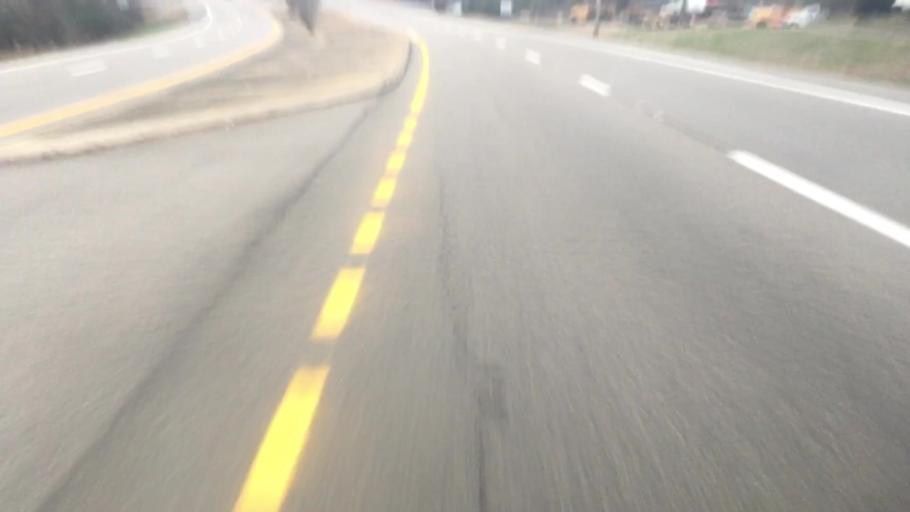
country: US
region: Alabama
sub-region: Jefferson County
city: Fultondale
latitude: 33.5784
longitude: -86.8051
